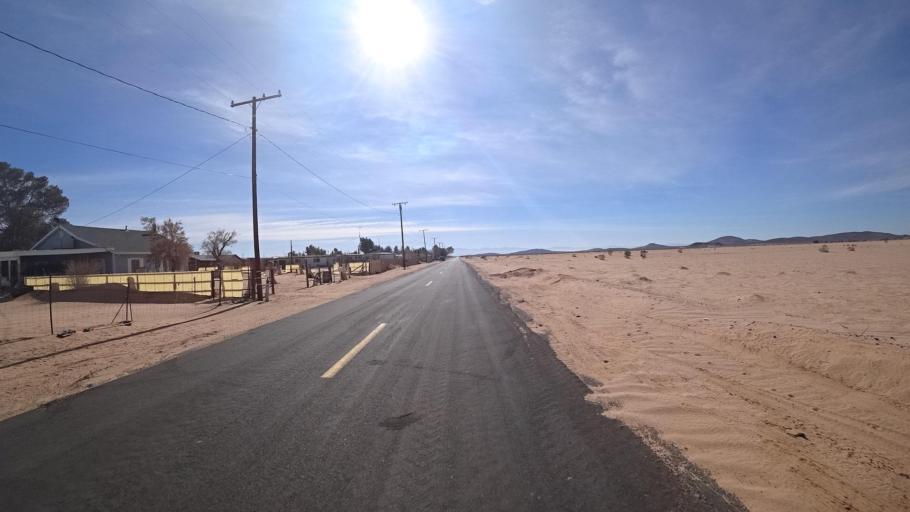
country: US
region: California
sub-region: Kern County
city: North Edwards
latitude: 35.0939
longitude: -117.7927
